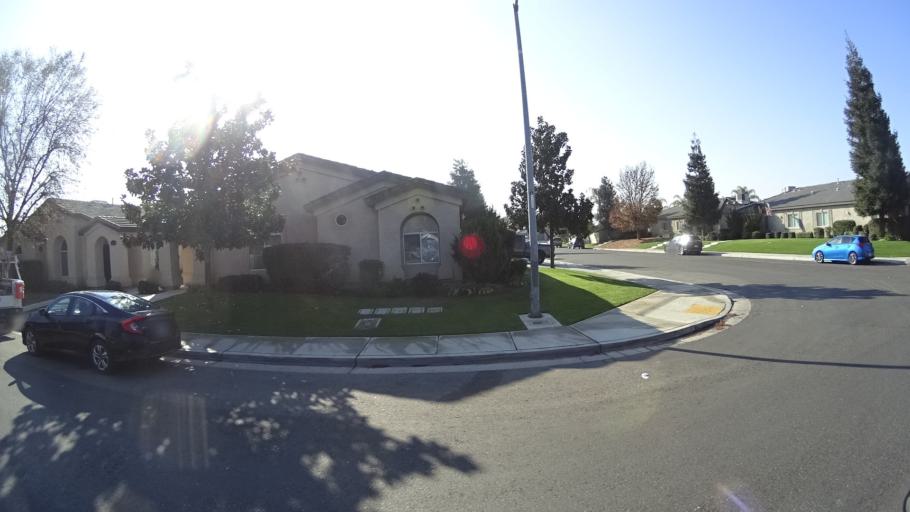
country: US
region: California
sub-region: Kern County
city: Greenacres
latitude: 35.3101
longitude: -119.1106
